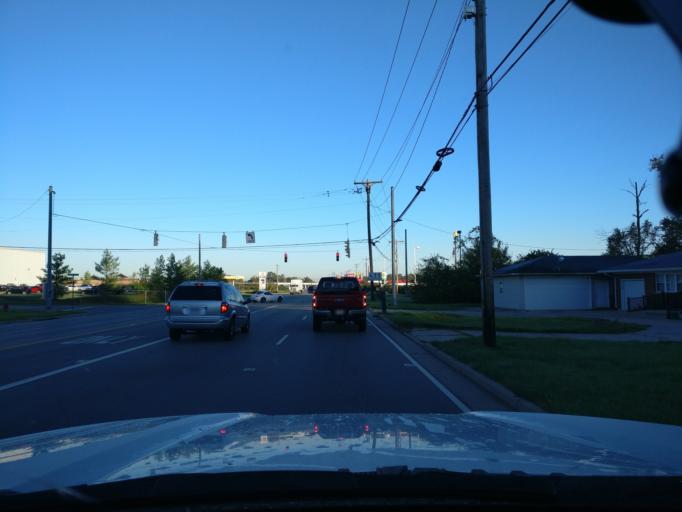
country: US
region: Ohio
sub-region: Warren County
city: Franklin
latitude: 39.5386
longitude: -84.2892
